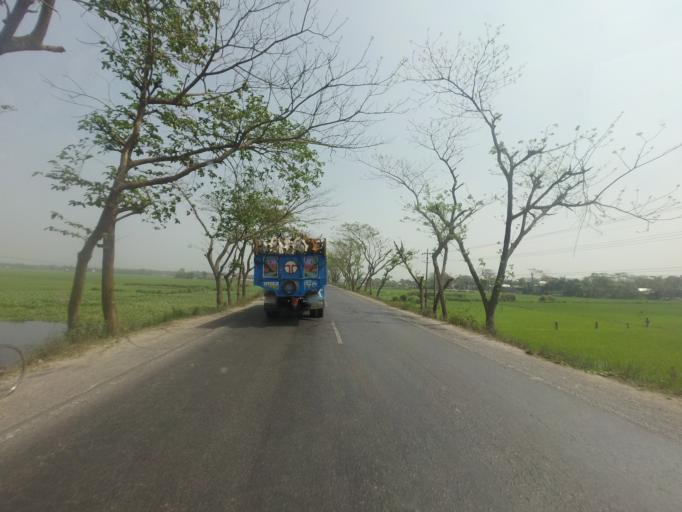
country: BD
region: Dhaka
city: Bhairab Bazar
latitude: 24.0484
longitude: 91.0975
